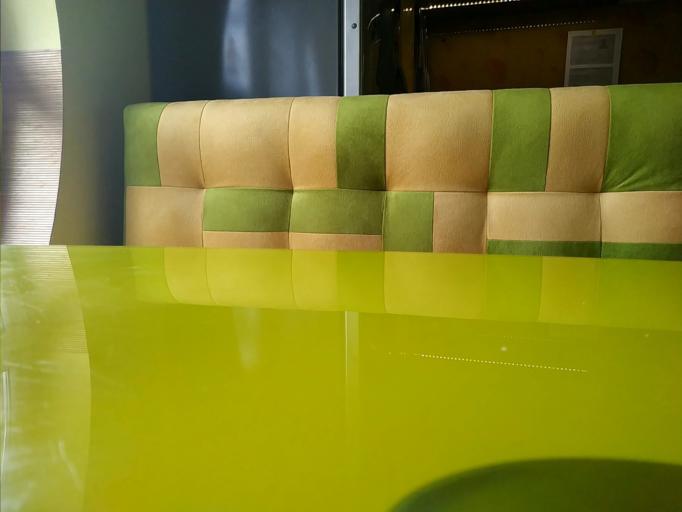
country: RU
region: Pskov
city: Plyussa
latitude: 58.3975
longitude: 29.6967
